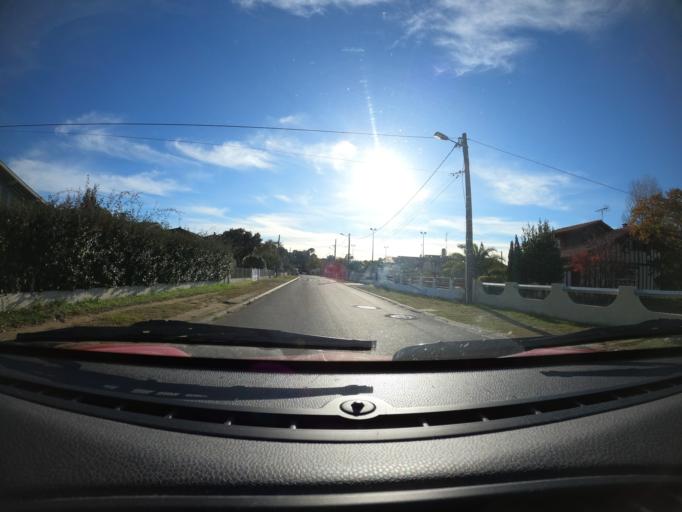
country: FR
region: Aquitaine
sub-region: Departement des Landes
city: Ondres
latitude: 43.5694
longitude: -1.4498
